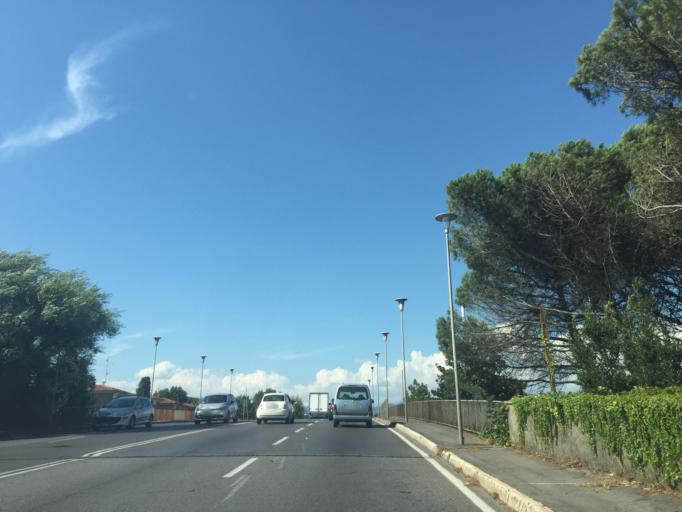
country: IT
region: Tuscany
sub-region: Provincia di Lucca
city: Lucca
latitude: 43.8372
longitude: 10.4950
